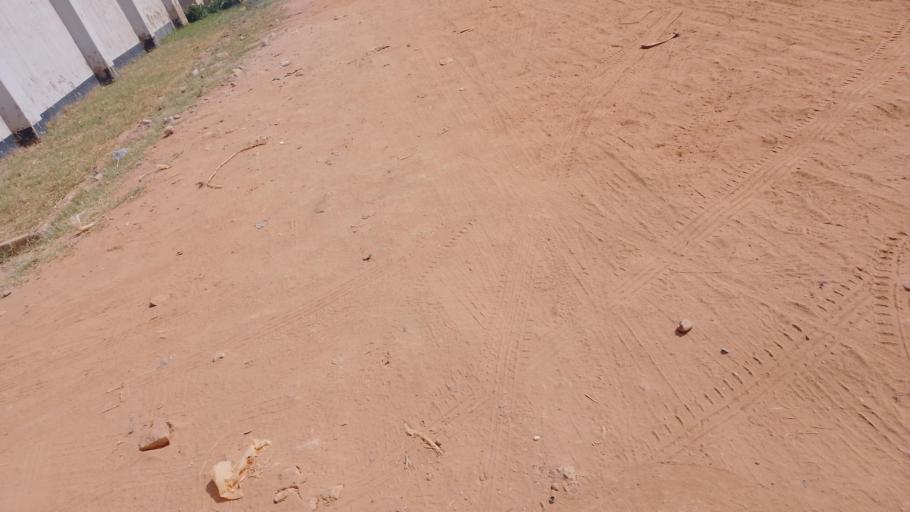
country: ZM
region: Lusaka
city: Lusaka
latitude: -15.3931
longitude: 28.3916
